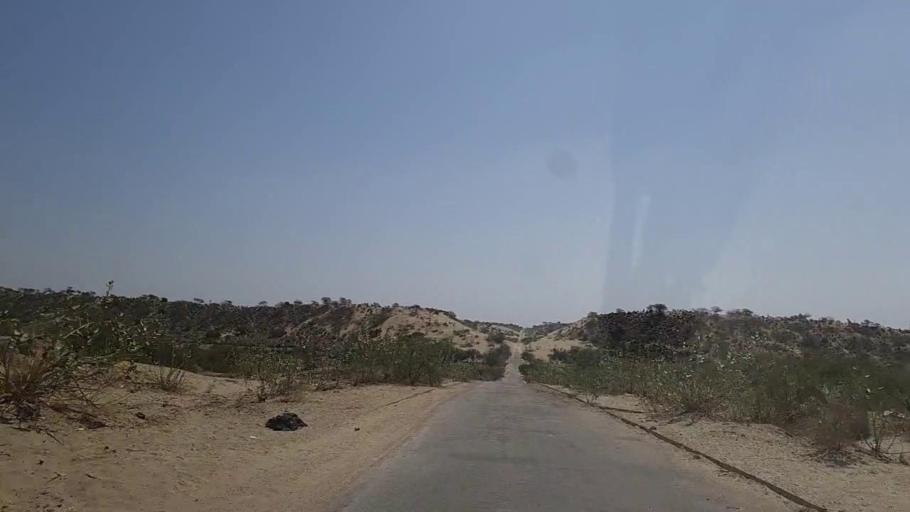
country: PK
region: Sindh
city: Diplo
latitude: 24.5122
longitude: 69.4205
